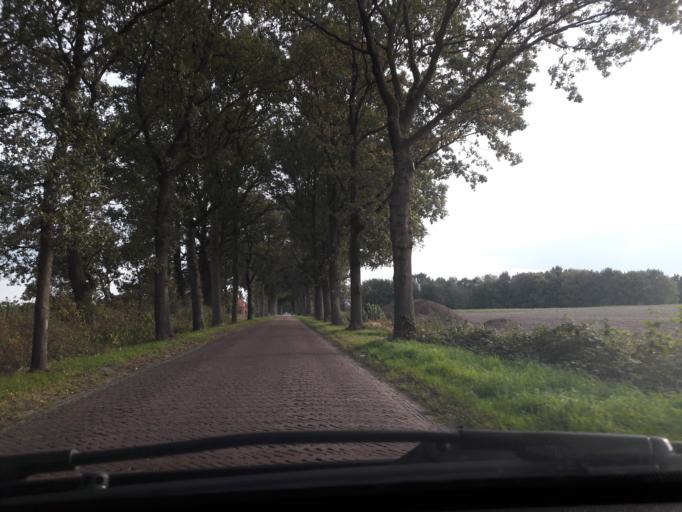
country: NL
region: Drenthe
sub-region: Gemeente Borger-Odoorn
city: Borger
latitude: 52.9568
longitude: 6.8242
